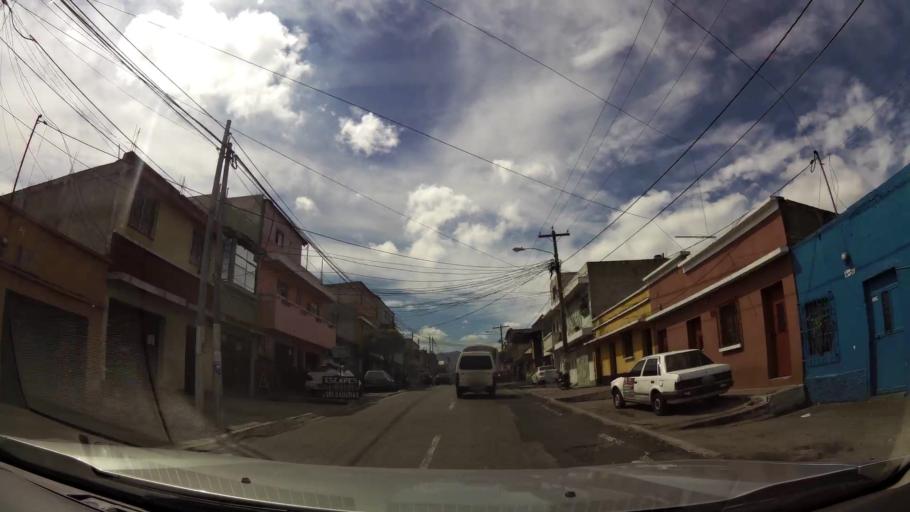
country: GT
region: Guatemala
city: Mixco
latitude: 14.6590
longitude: -90.5765
